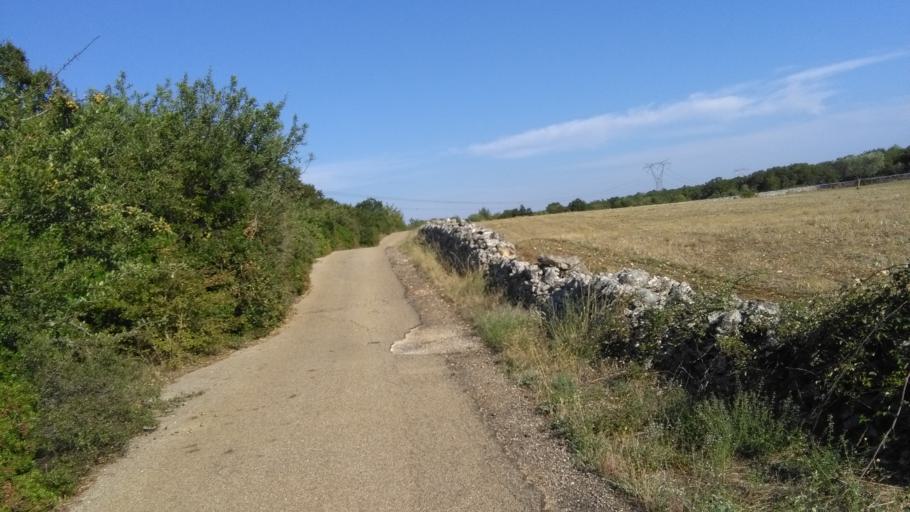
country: IT
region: Apulia
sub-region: Provincia di Bari
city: Putignano
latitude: 40.8189
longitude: 17.0541
